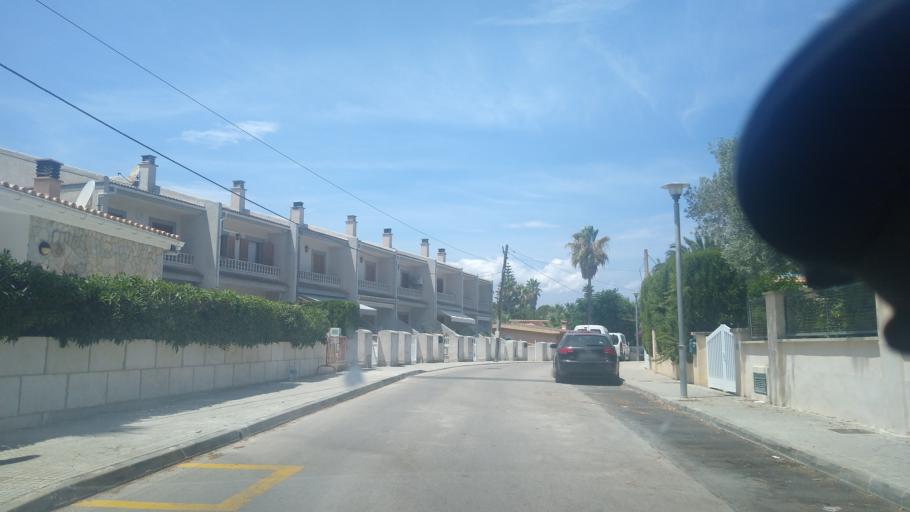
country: ES
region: Balearic Islands
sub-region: Illes Balears
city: Santa Margalida
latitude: 39.7582
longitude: 3.1654
